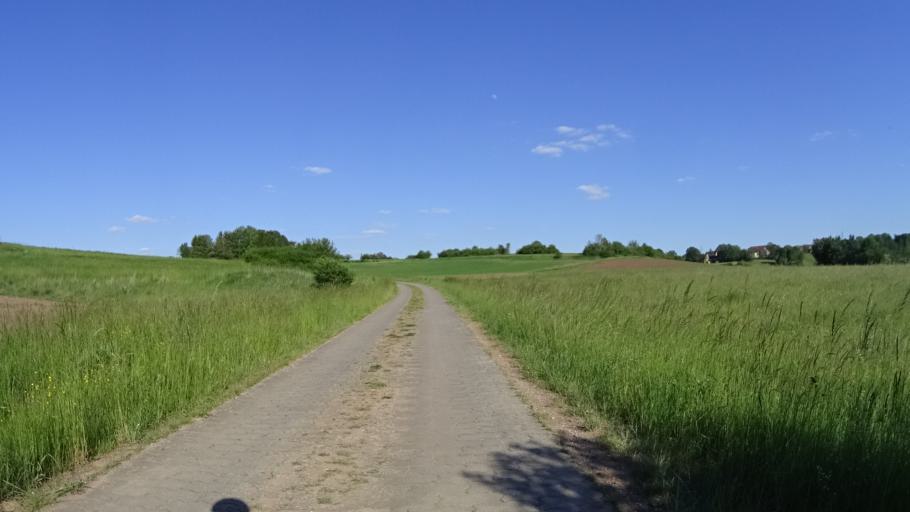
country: DE
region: Bavaria
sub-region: Regierungsbezirk Mittelfranken
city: Lichtenau
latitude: 49.1624
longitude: 10.3593
